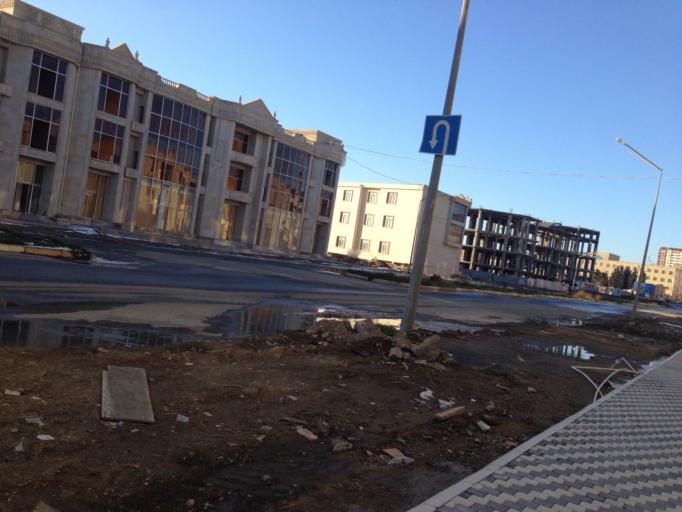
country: AZ
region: Baki
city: Baku
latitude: 40.4122
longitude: 49.8575
